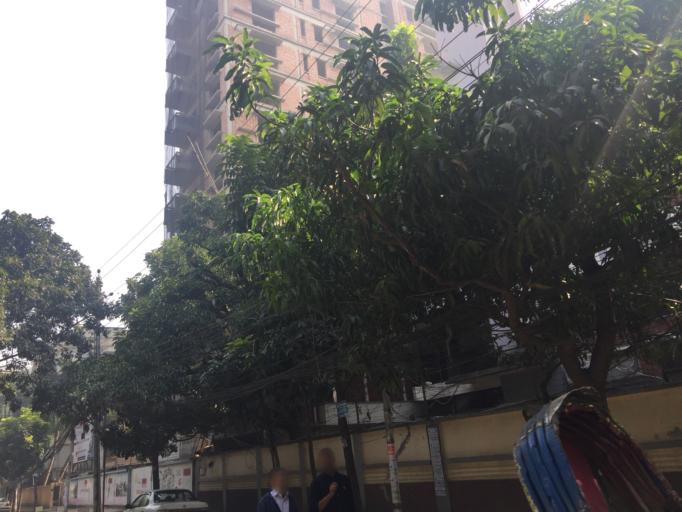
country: BD
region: Dhaka
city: Azimpur
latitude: 23.7419
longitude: 90.3785
